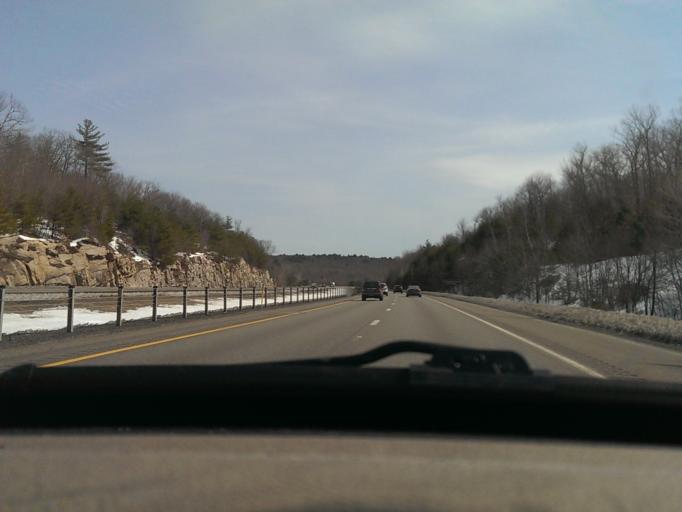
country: US
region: Massachusetts
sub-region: Worcester County
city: Whitinsville
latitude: 42.1390
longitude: -71.7109
